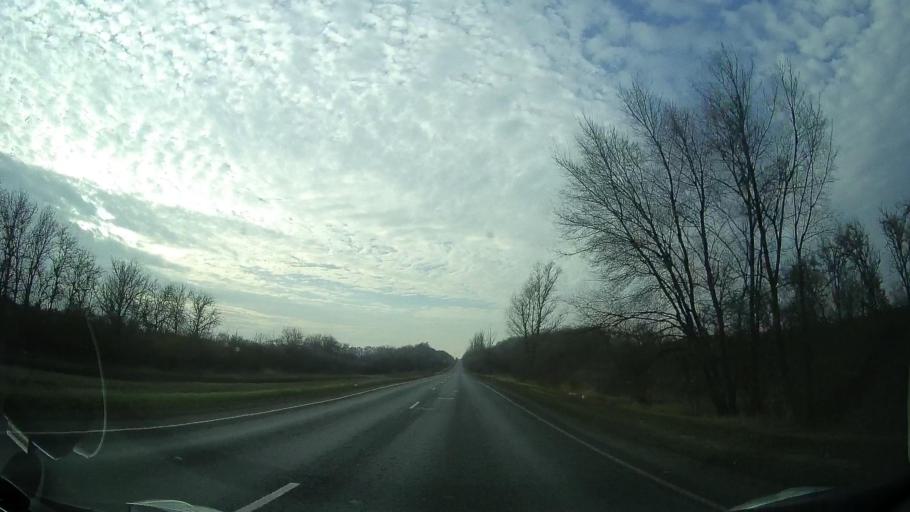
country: RU
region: Rostov
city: Bagayevskaya
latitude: 47.0959
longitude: 40.3062
